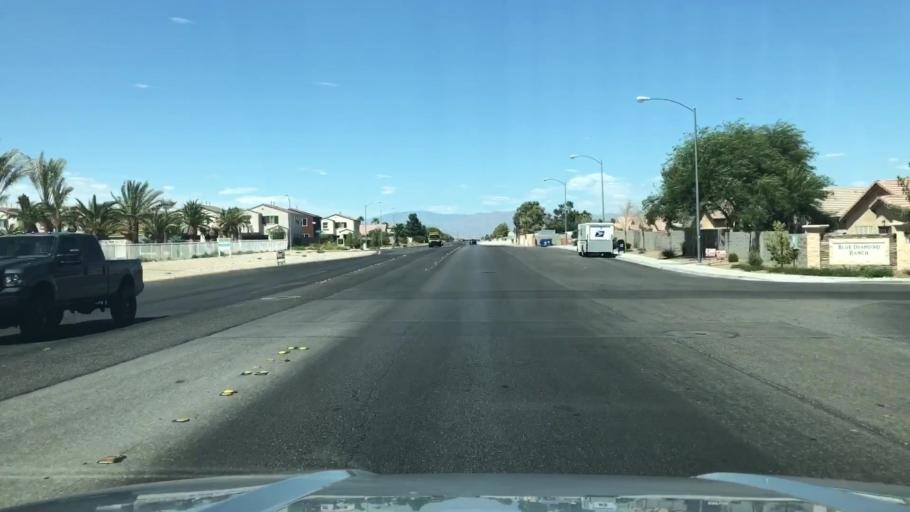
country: US
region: Nevada
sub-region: Clark County
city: Enterprise
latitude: 36.0450
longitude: -115.2078
